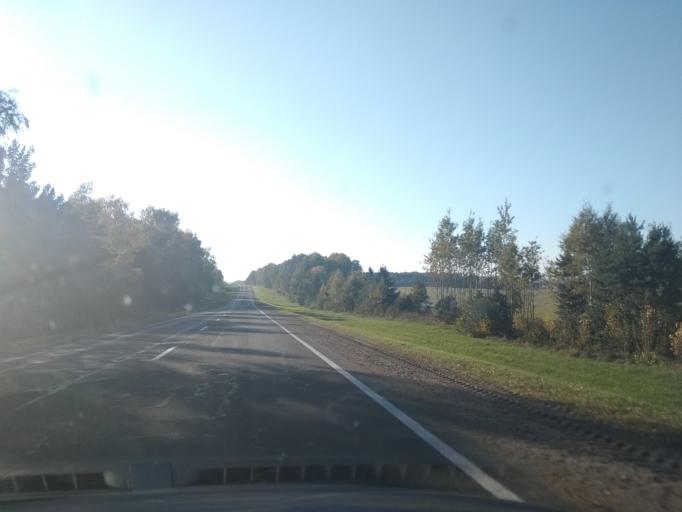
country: BY
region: Grodnenskaya
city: Svislach
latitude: 53.1273
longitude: 24.1329
